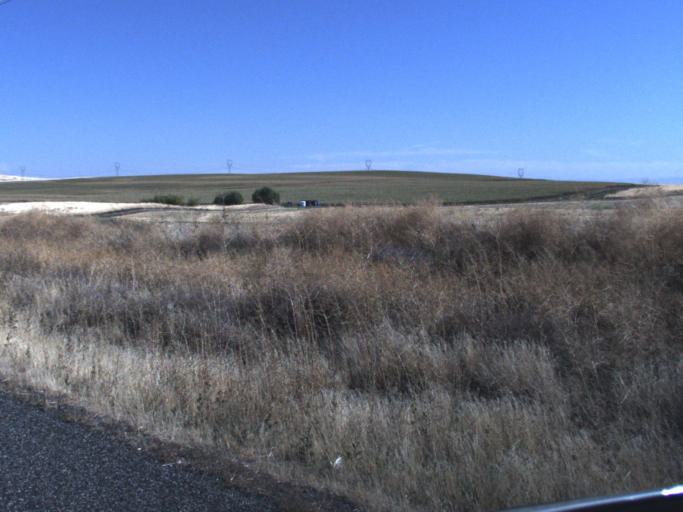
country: US
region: Washington
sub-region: Walla Walla County
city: Burbank
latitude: 46.2799
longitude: -118.7541
